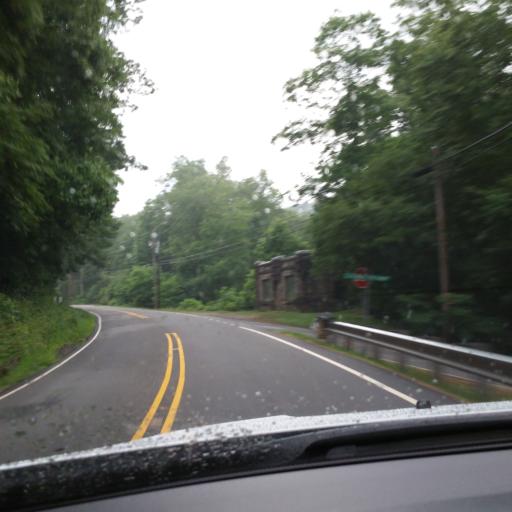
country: US
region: North Carolina
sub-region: Yancey County
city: Burnsville
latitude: 35.7703
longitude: -82.1975
